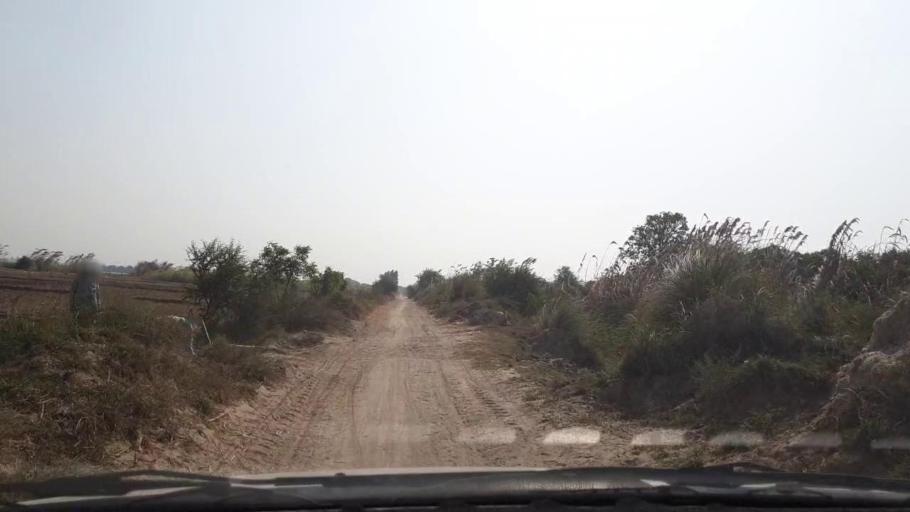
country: PK
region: Sindh
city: Tando Muhammad Khan
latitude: 25.0862
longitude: 68.3588
